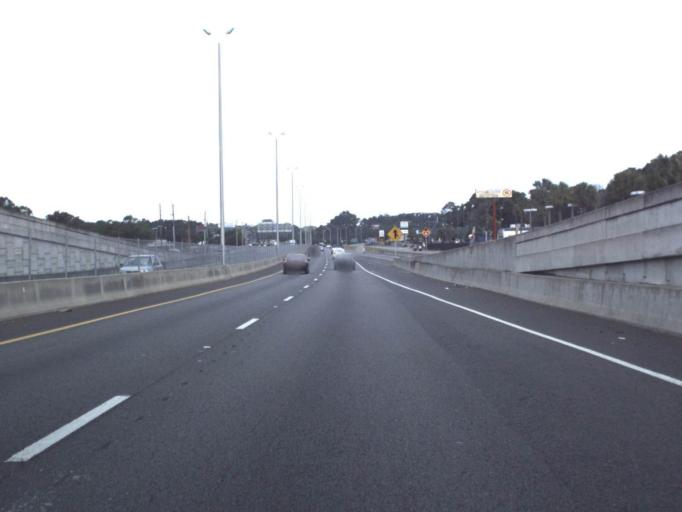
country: US
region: Florida
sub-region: Duval County
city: Jacksonville
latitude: 30.3246
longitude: -81.5625
